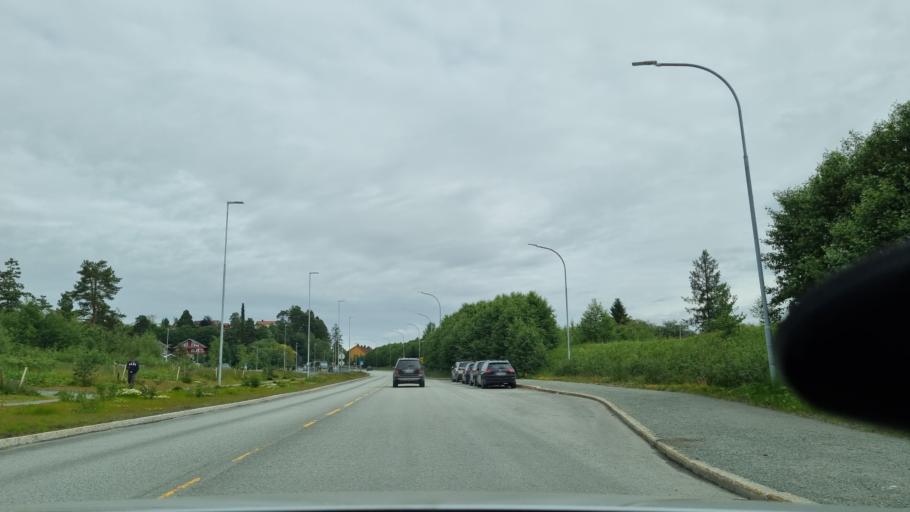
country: NO
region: Sor-Trondelag
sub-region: Melhus
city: Melhus
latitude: 63.3486
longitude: 10.3306
